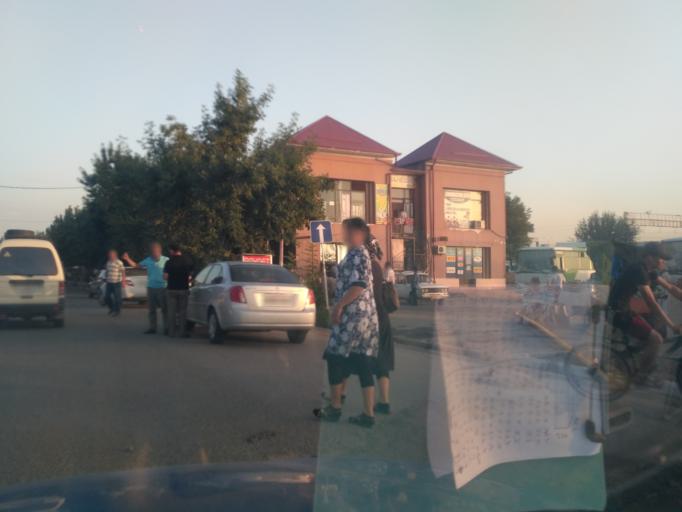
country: UZ
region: Sirdaryo
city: Guliston
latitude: 40.4958
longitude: 68.7661
